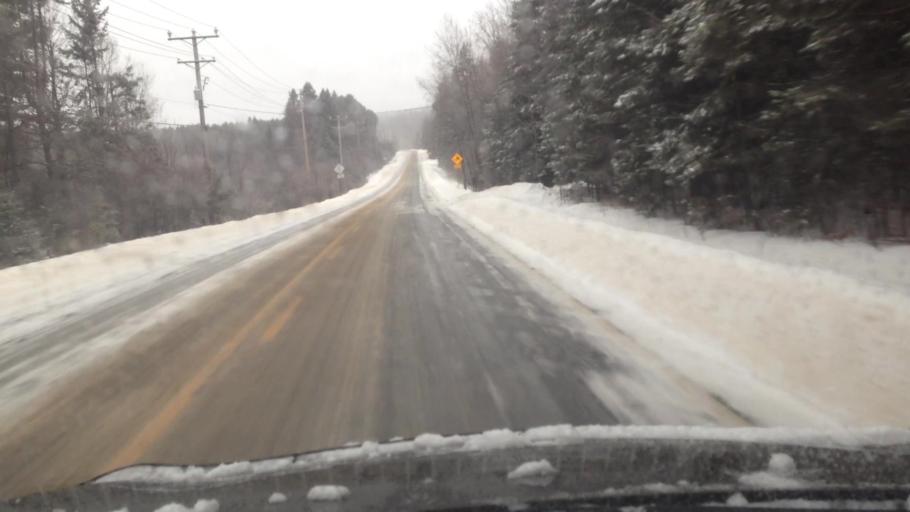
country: CA
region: Quebec
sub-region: Laurentides
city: Mont-Tremblant
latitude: 46.0032
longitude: -74.6214
